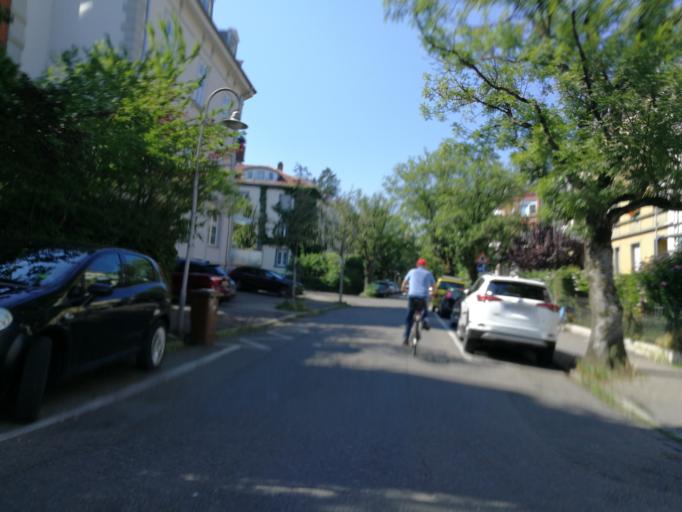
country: DE
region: Baden-Wuerttemberg
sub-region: Freiburg Region
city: Konstanz
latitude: 47.6605
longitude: 9.1696
